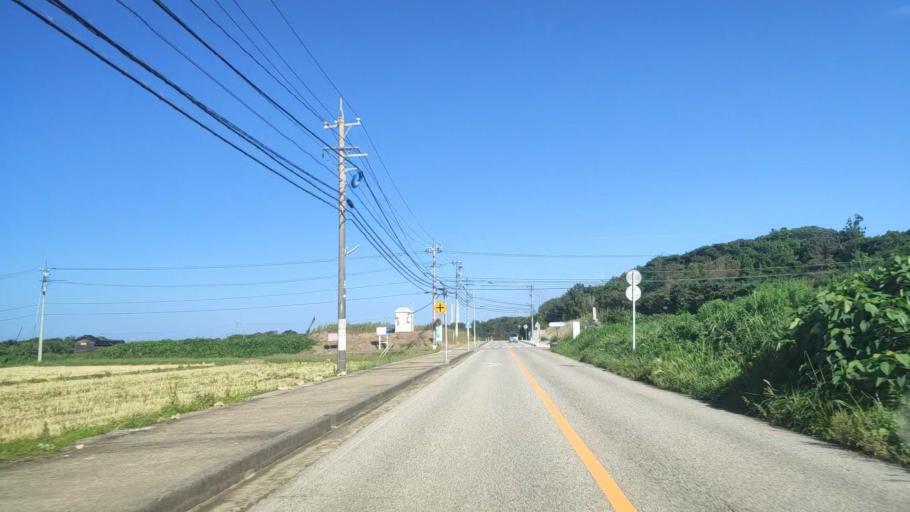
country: JP
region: Ishikawa
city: Hakui
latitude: 37.0475
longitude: 136.7373
